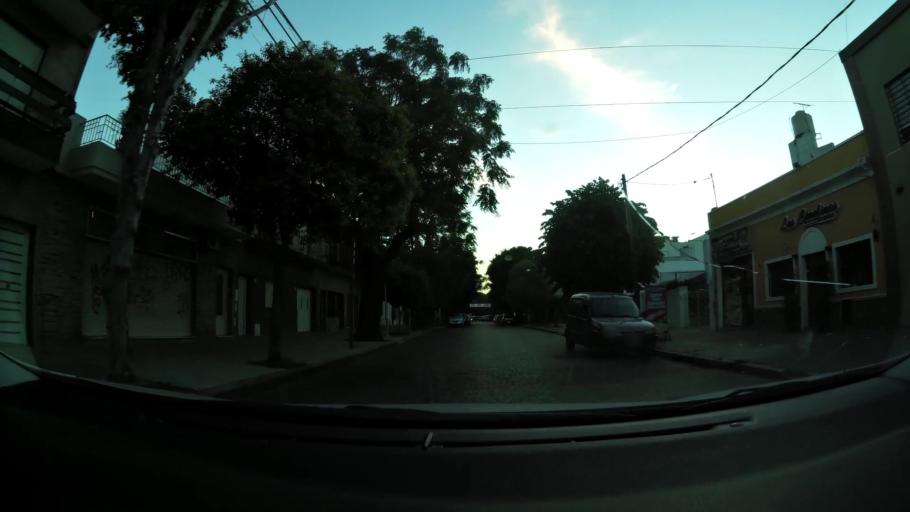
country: AR
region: Buenos Aires F.D.
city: Villa Lugano
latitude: -34.6771
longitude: -58.4739
